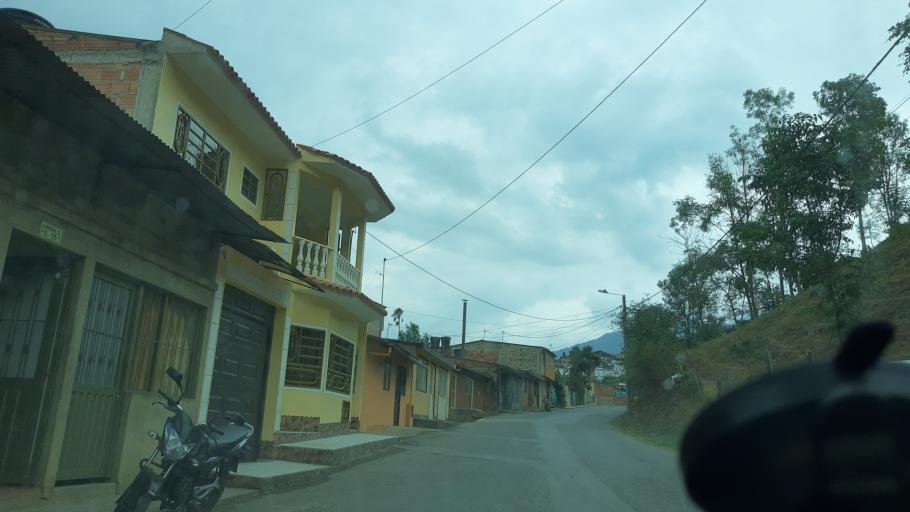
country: CO
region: Boyaca
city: Garagoa
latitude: 5.0795
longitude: -73.3670
